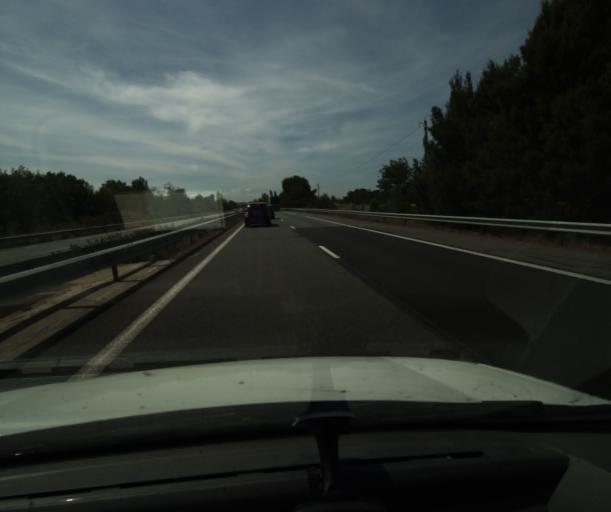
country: FR
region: Languedoc-Roussillon
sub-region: Departement de l'Aude
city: Villepinte
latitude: 43.2489
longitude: 2.0628
